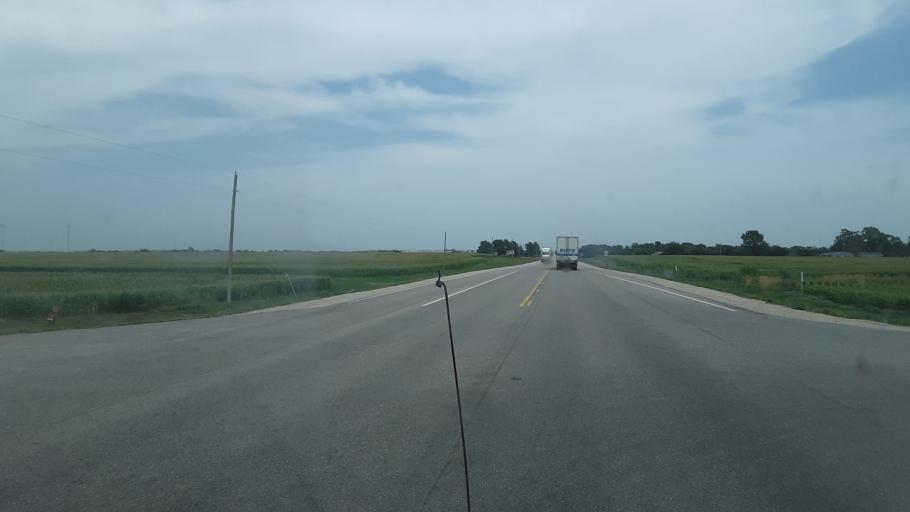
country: US
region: Kansas
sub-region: Allen County
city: Iola
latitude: 37.9219
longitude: -95.2813
